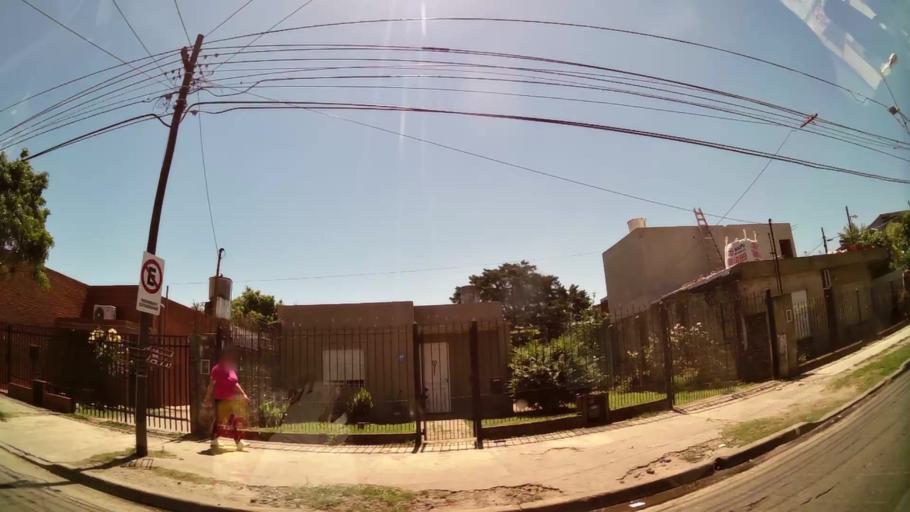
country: AR
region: Buenos Aires
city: Hurlingham
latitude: -34.4937
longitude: -58.6709
